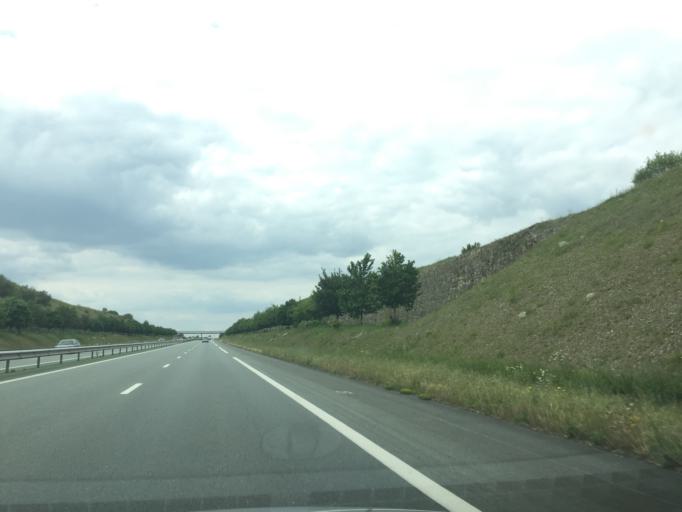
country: FR
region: Poitou-Charentes
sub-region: Departement des Deux-Sevres
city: Saint-Maxire
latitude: 46.4233
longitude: -0.4564
